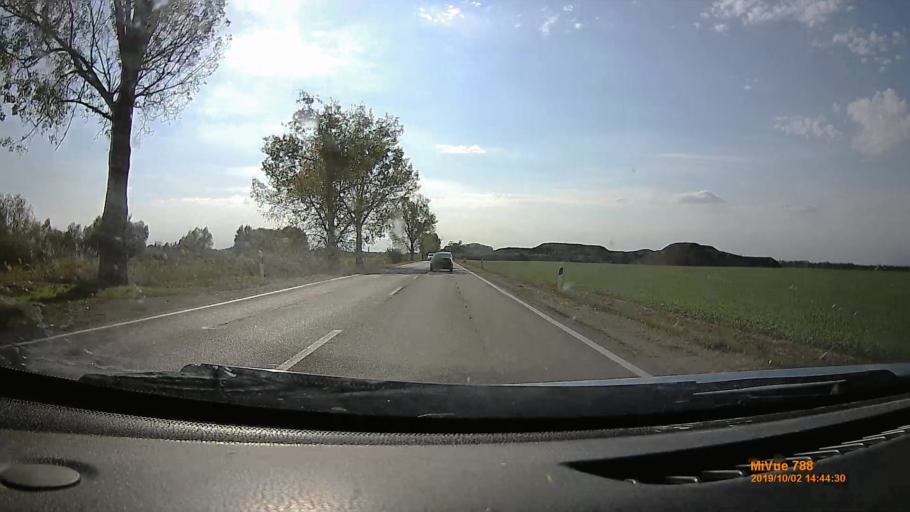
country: HU
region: Heves
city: Szihalom
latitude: 47.7668
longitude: 20.4520
